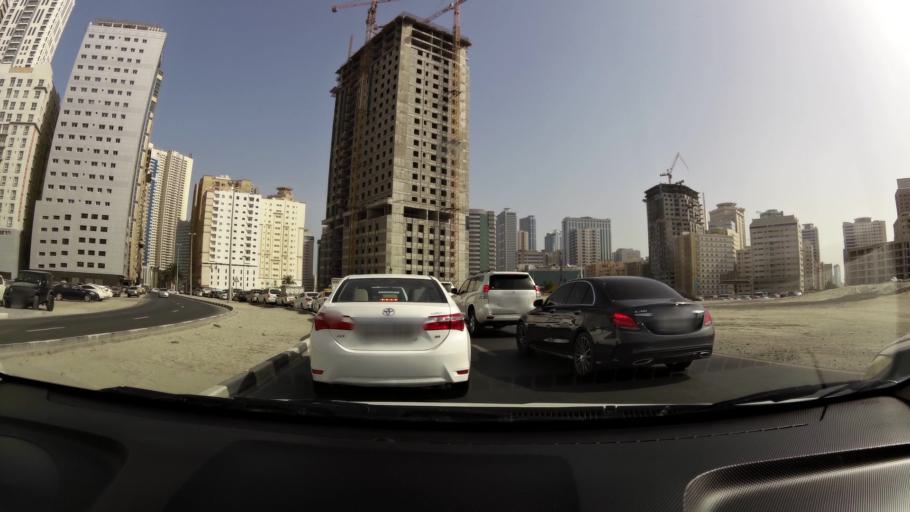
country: AE
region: Ash Shariqah
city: Sharjah
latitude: 25.3141
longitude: 55.3798
